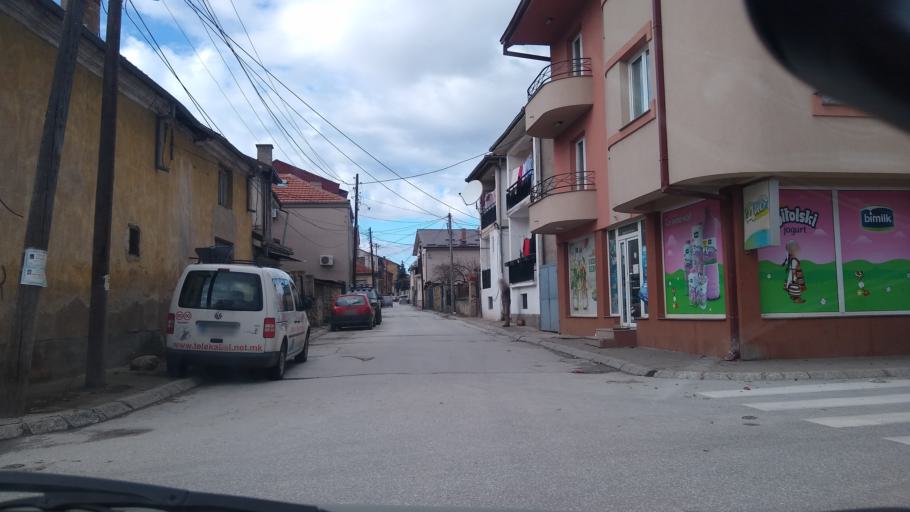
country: MK
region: Bitola
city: Bitola
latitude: 41.0283
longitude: 21.3261
